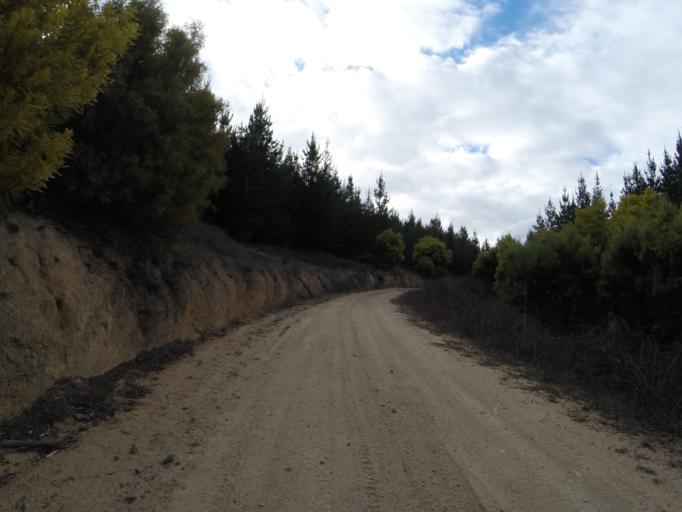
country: AU
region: Australian Capital Territory
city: Macquarie
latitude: -35.3494
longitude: 148.9500
